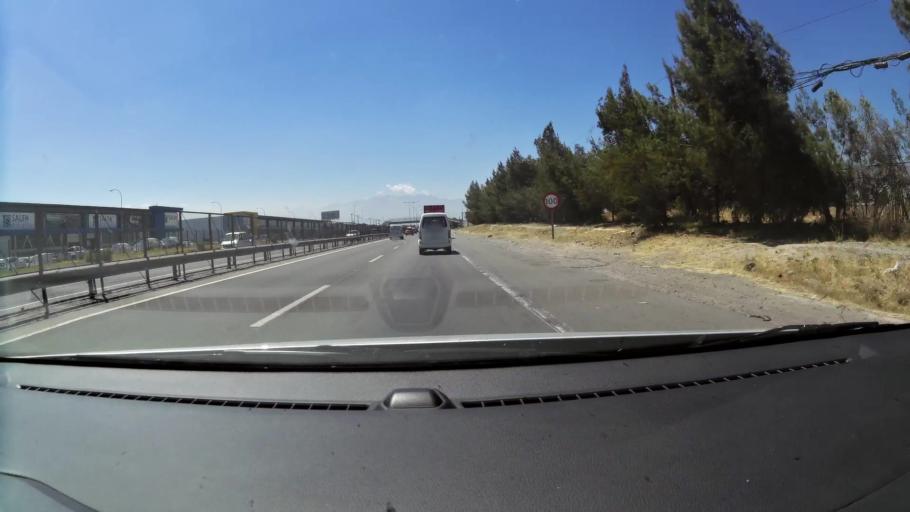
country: CL
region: Santiago Metropolitan
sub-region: Provincia de Santiago
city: Lo Prado
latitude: -33.4445
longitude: -70.7856
